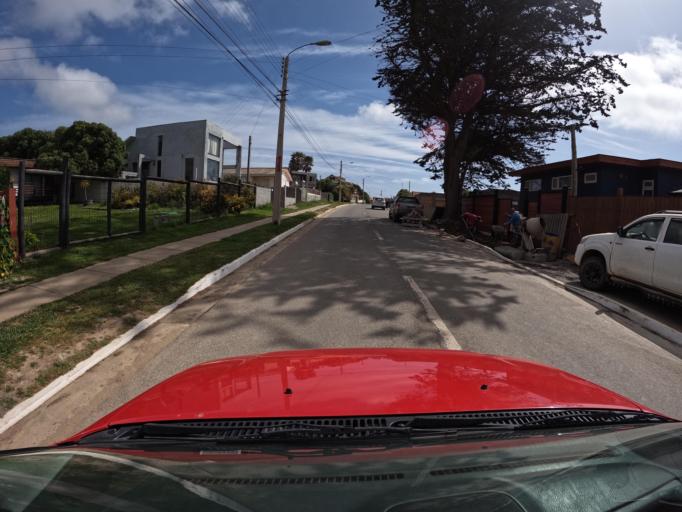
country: CL
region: O'Higgins
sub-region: Provincia de Colchagua
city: Santa Cruz
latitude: -34.3889
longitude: -72.0186
